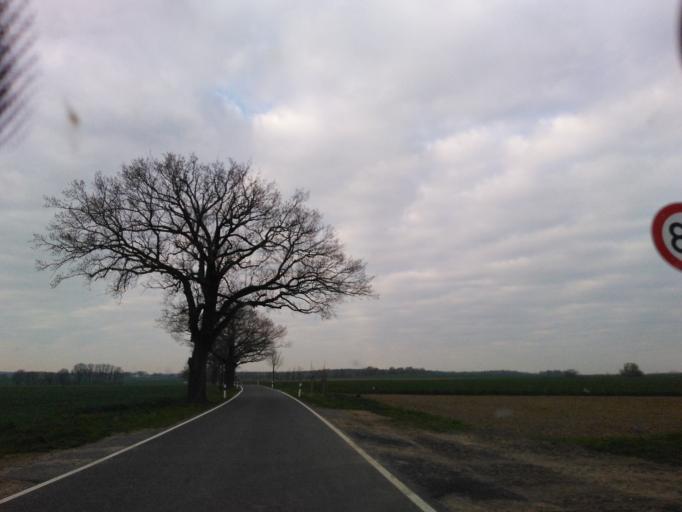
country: DE
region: Brandenburg
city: Buckow
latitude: 52.6420
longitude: 14.0777
